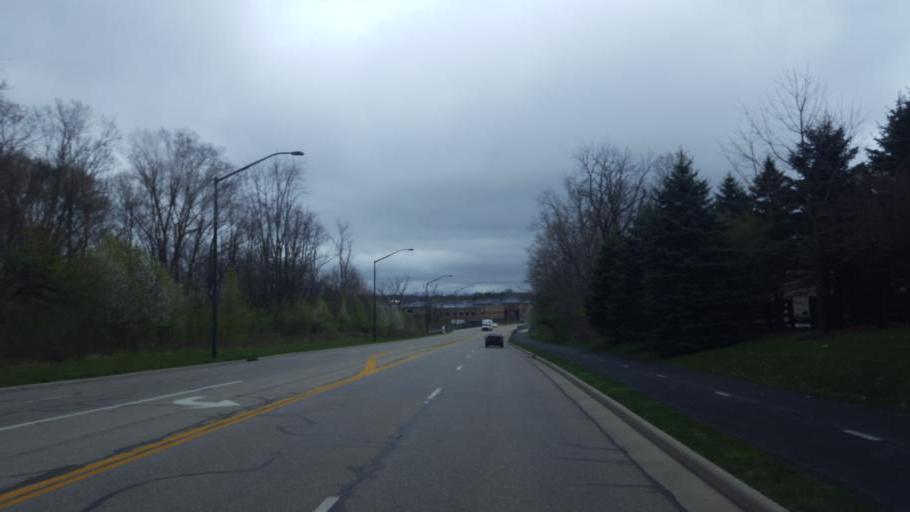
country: US
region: Ohio
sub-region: Franklin County
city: Westerville
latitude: 40.1380
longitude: -82.9551
